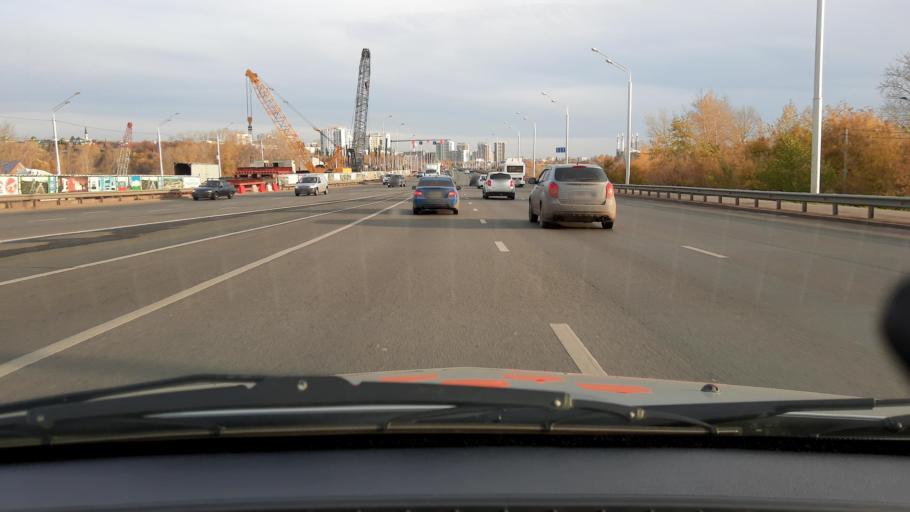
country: RU
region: Bashkortostan
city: Ufa
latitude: 54.7000
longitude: 55.9531
